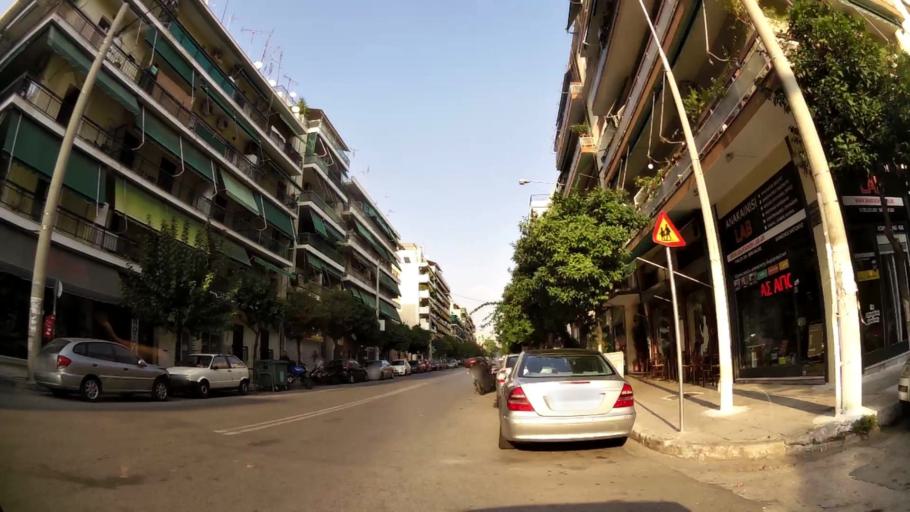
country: GR
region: Attica
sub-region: Nomarchia Athinas
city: Kallithea
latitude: 37.9543
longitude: 23.7074
